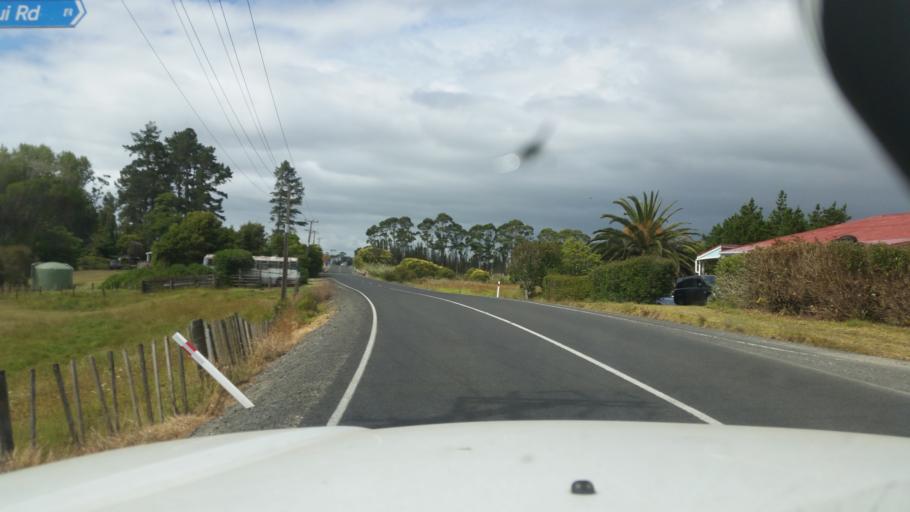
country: NZ
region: Northland
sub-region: Far North District
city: Ahipara
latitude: -35.1754
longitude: 173.1775
